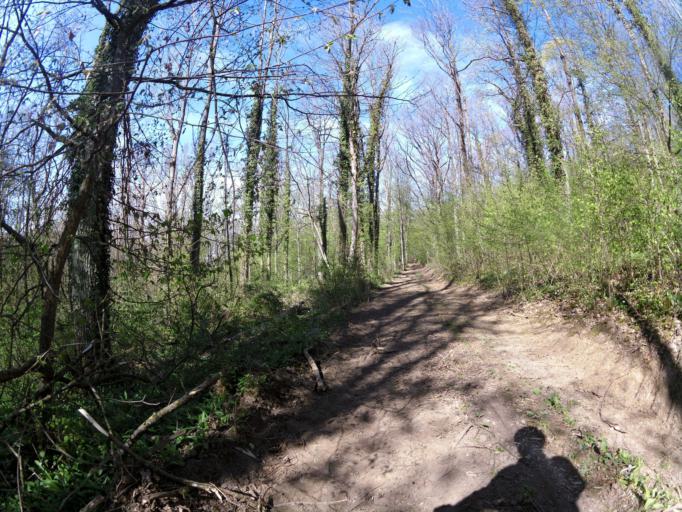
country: DE
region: Bavaria
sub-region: Regierungsbezirk Unterfranken
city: Winterhausen
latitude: 49.6964
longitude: 10.0020
